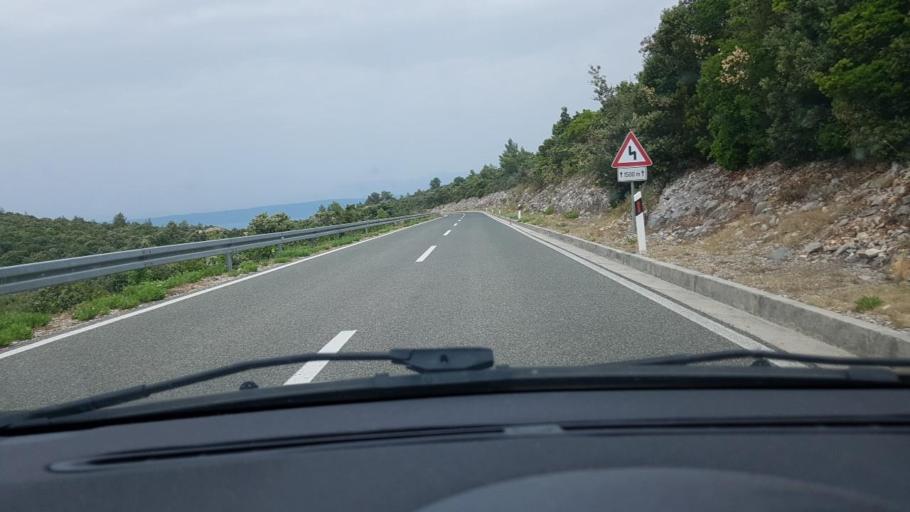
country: HR
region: Dubrovacko-Neretvanska
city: Smokvica
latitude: 42.9523
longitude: 16.9424
